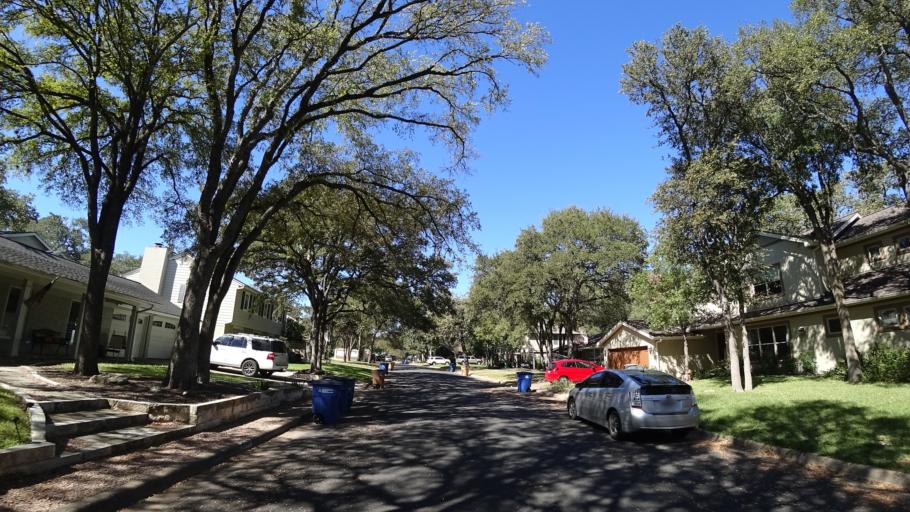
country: US
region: Texas
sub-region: Travis County
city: West Lake Hills
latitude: 30.3639
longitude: -97.7678
